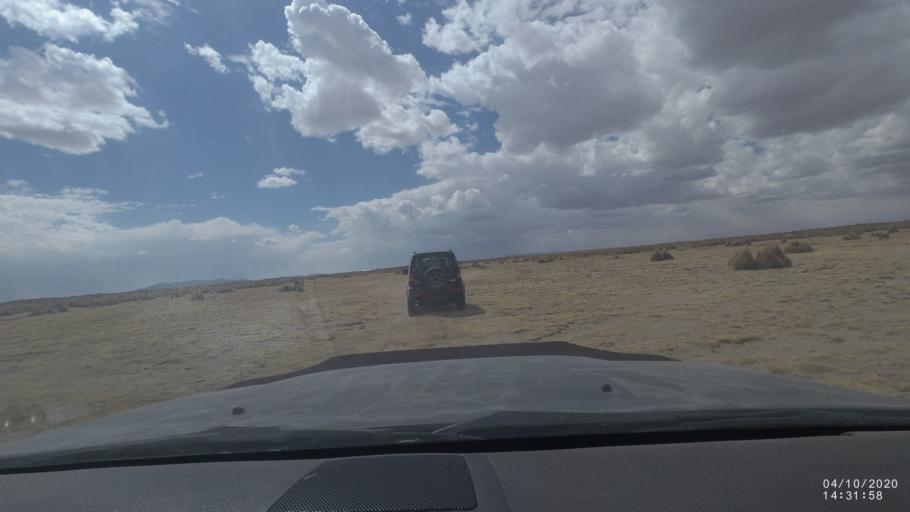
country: BO
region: Oruro
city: Poopo
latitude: -18.6739
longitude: -67.4639
